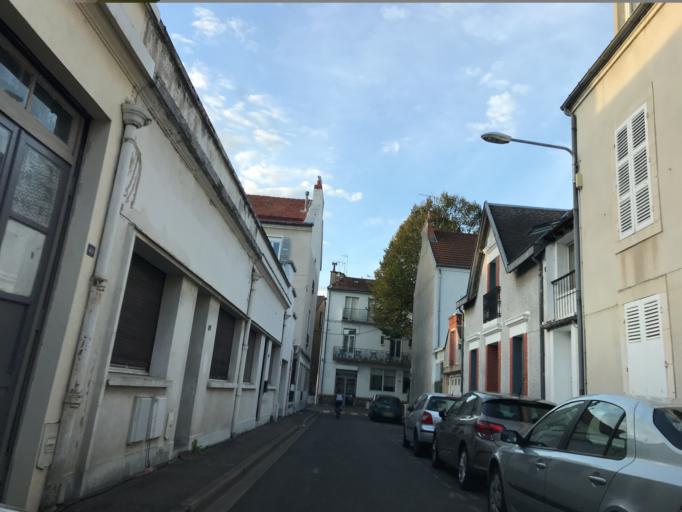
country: FR
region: Auvergne
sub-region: Departement de l'Allier
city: Vichy
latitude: 46.1224
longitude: 3.4297
